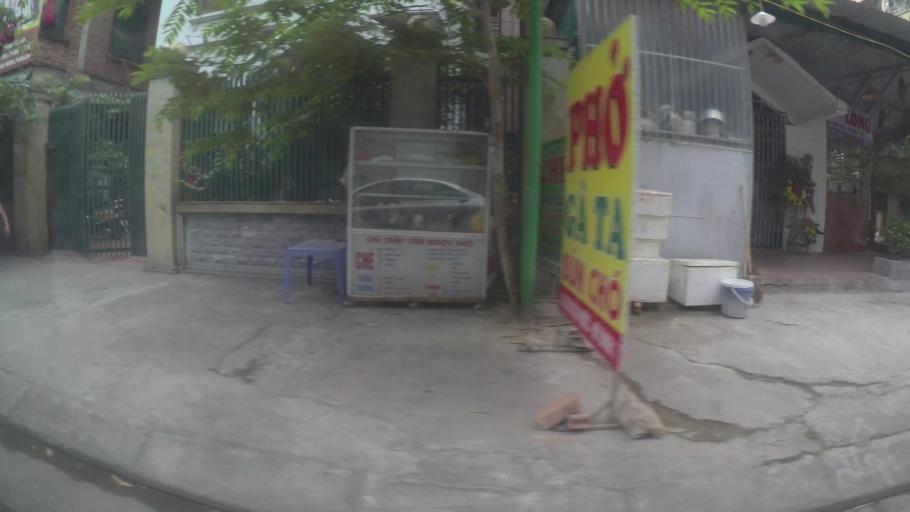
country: VN
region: Ha Noi
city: Cau Dien
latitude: 21.0325
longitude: 105.7618
